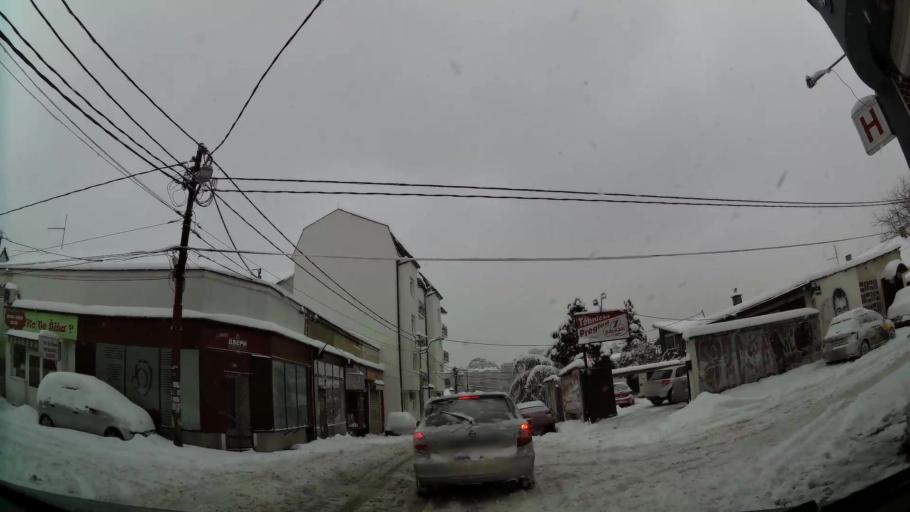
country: RS
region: Central Serbia
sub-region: Belgrade
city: Vracar
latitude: 44.7907
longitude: 20.4893
